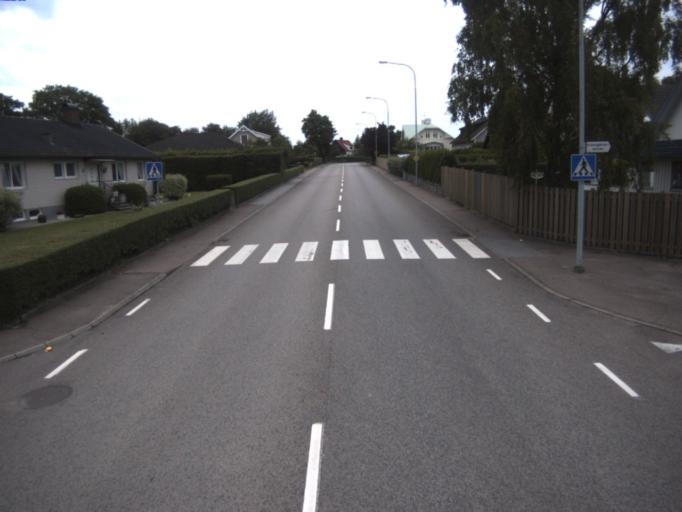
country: SE
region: Skane
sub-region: Helsingborg
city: Odakra
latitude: 56.1027
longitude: 12.7530
